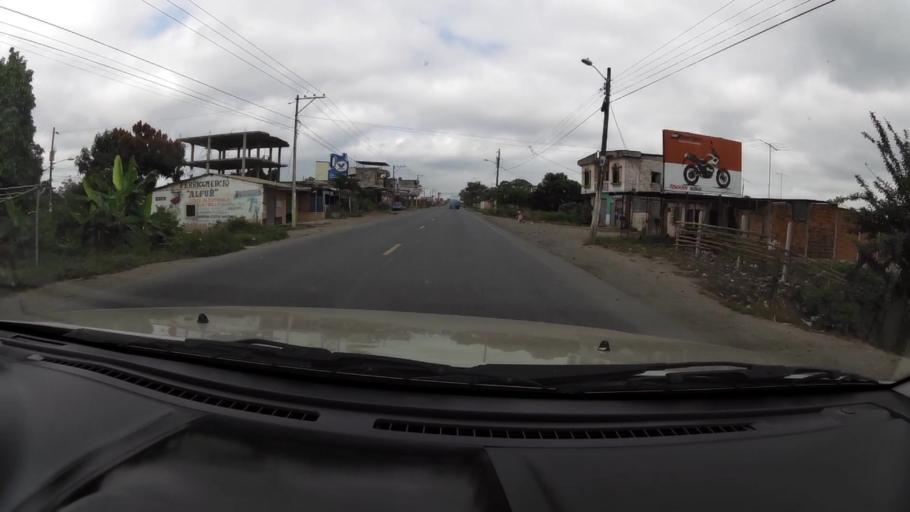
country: EC
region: Guayas
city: Naranjal
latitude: -2.6844
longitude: -79.6273
